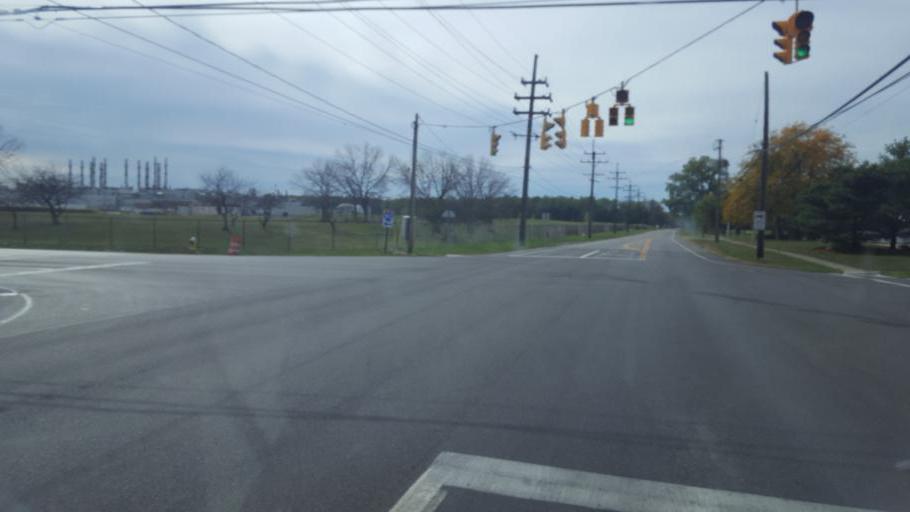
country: US
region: Ohio
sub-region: Lorain County
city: Avon Lake
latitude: 41.4935
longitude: -82.0614
